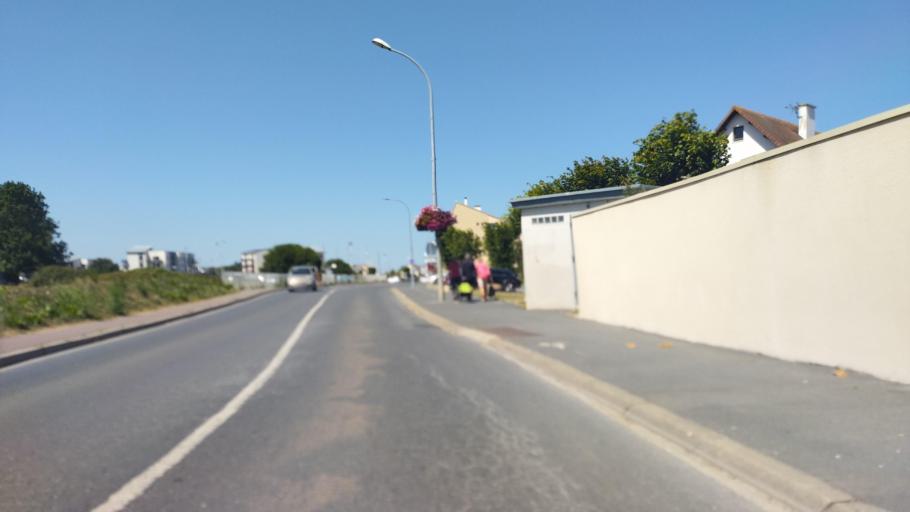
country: FR
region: Lower Normandy
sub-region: Departement du Calvados
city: Courseulles-sur-Mer
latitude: 49.3309
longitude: -0.4614
